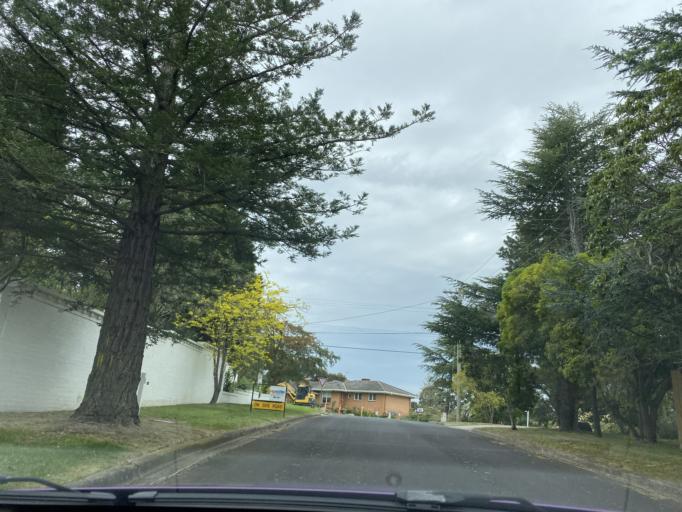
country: AU
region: Victoria
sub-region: Manningham
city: Templestowe Lower
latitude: -37.7651
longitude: 145.1394
